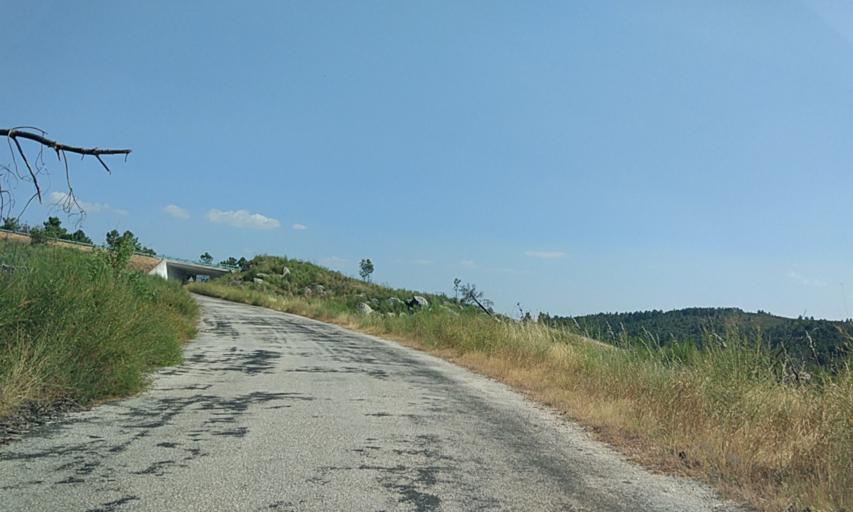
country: PT
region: Vila Real
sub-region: Sabrosa
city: Sabrosa
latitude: 41.3028
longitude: -7.4860
